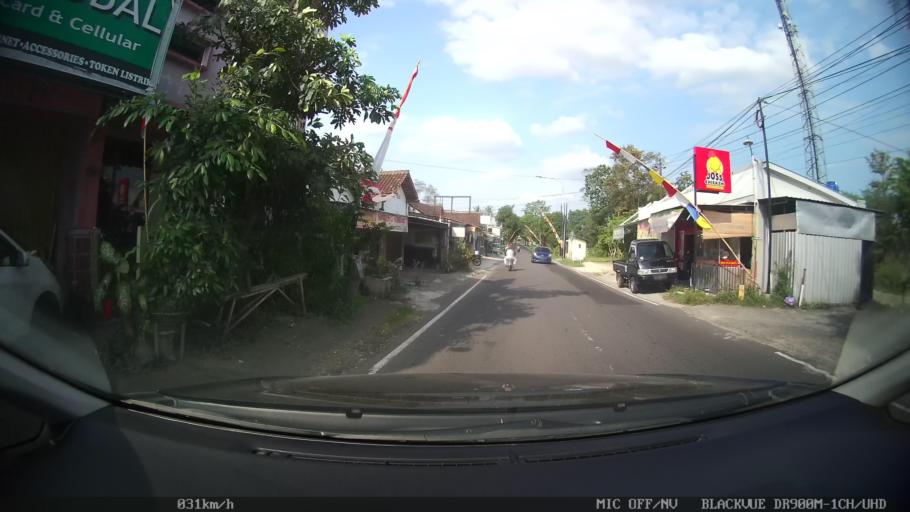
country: ID
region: Daerah Istimewa Yogyakarta
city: Depok
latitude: -7.7229
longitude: 110.4355
